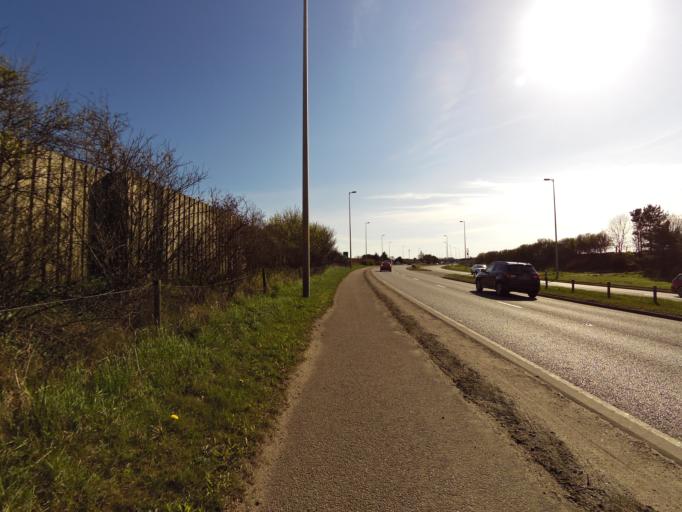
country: GB
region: Scotland
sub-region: Aberdeenshire
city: Newtonhill
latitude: 57.0349
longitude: -2.1538
